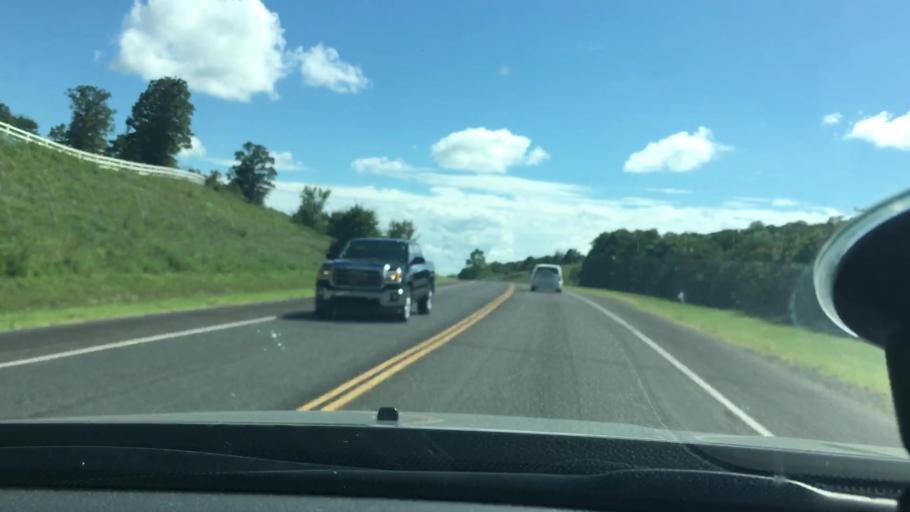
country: US
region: Oklahoma
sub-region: Sequoyah County
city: Vian
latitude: 35.5271
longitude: -94.9744
